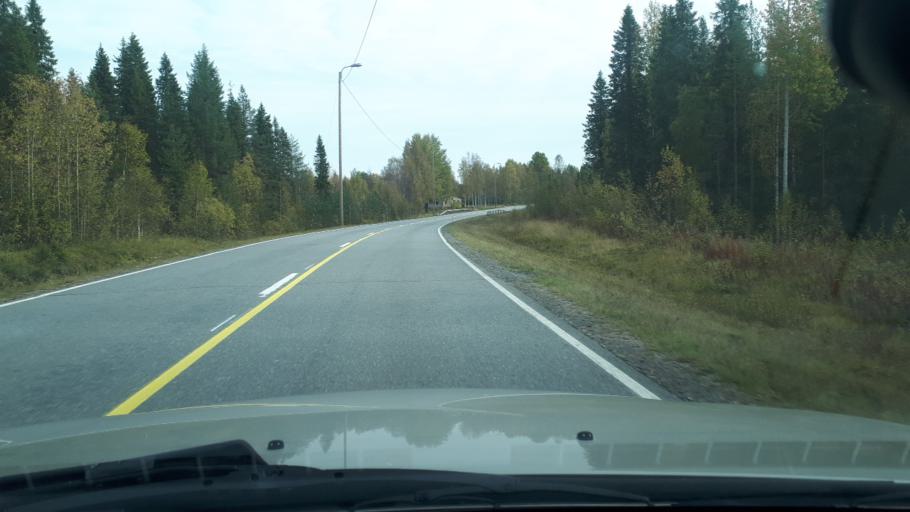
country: FI
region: Lapland
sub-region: Rovaniemi
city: Ranua
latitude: 66.0008
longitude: 26.2216
